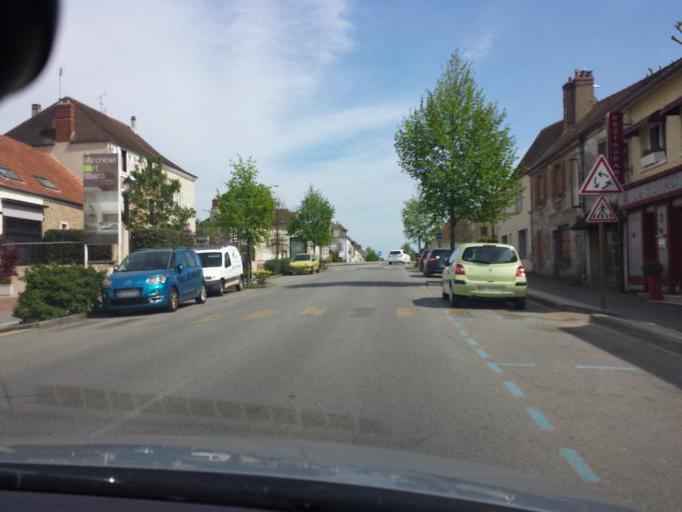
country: FR
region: Ile-de-France
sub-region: Departement des Yvelines
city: Neauphle-le-Chateau
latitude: 48.8029
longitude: 1.8994
